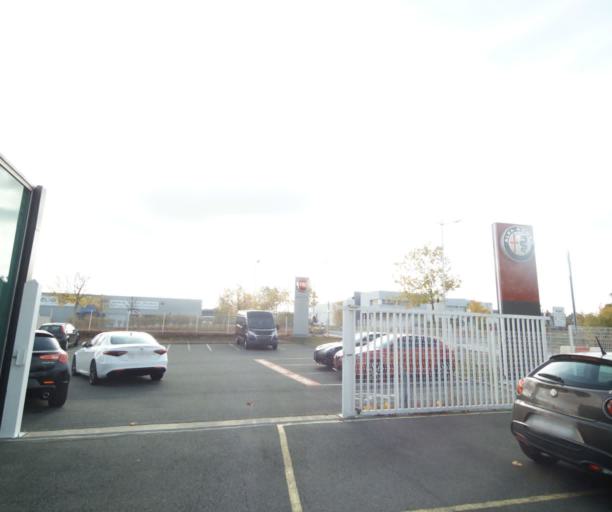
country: FR
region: Poitou-Charentes
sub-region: Departement de la Charente-Maritime
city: Saint-Georges-des-Coteaux
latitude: 45.7533
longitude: -0.6772
